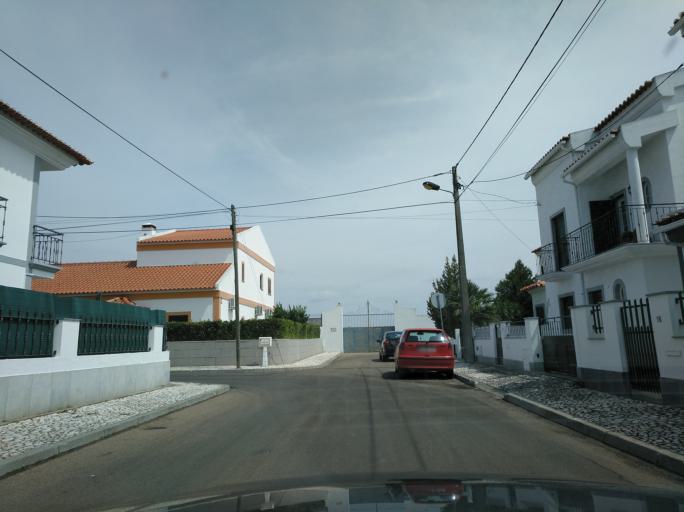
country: PT
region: Portalegre
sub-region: Campo Maior
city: Campo Maior
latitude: 39.0167
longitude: -7.0595
